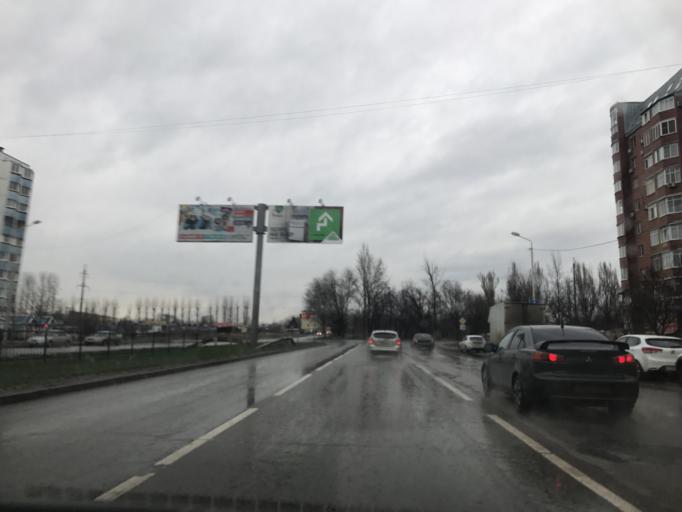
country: RU
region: Rostov
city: Severnyy
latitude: 47.2992
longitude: 39.7125
